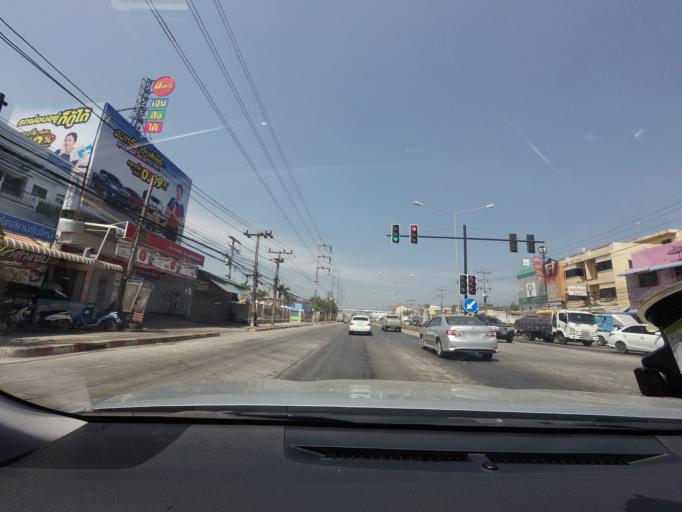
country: TH
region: Surat Thani
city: Surat Thani
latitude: 9.1483
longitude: 99.3930
